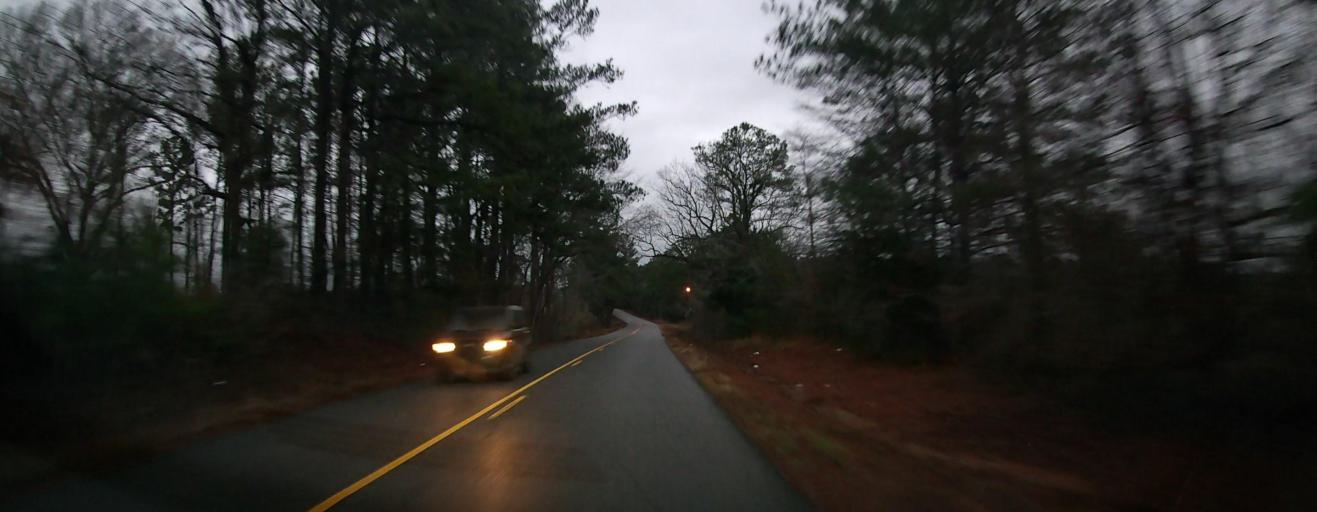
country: US
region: Alabama
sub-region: Tuscaloosa County
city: Vance
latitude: 33.1323
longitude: -87.2298
